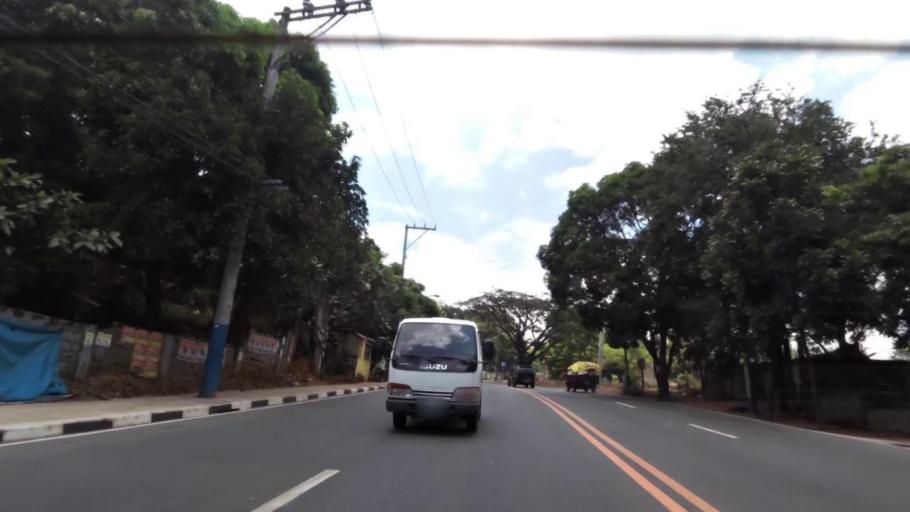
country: PH
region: Calabarzon
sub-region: Province of Rizal
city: Antipolo
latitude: 14.6100
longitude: 121.1599
